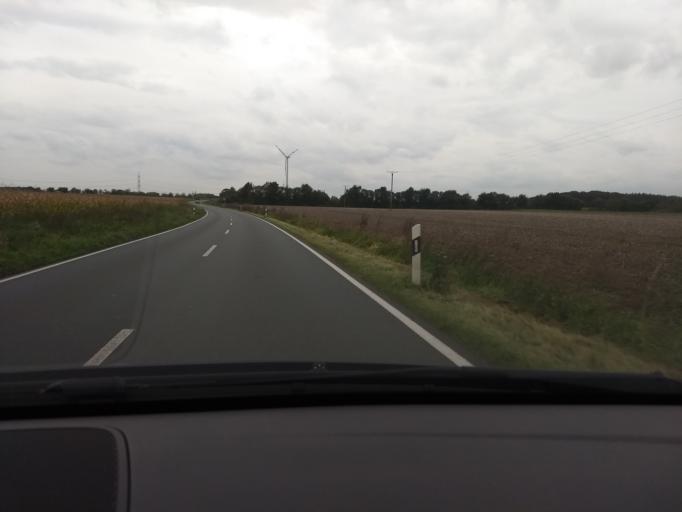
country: DE
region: North Rhine-Westphalia
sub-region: Regierungsbezirk Munster
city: Heiden
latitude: 51.8111
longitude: 6.9711
